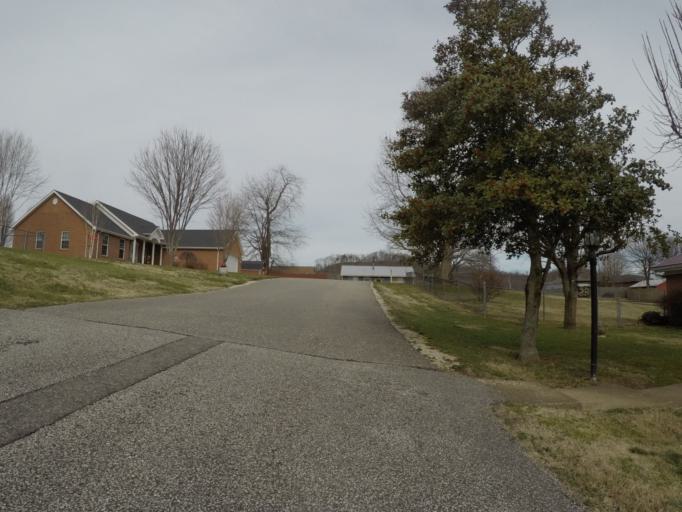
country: US
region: West Virginia
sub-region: Cabell County
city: Pea Ridge
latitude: 38.4527
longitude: -82.3418
